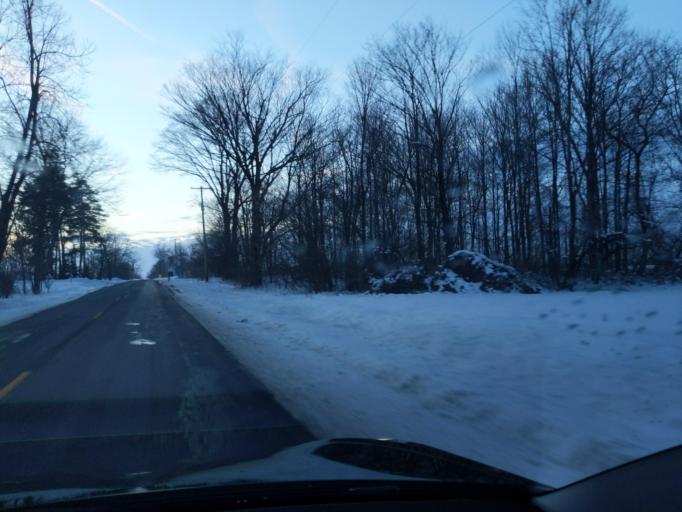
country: US
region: Michigan
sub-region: Ingham County
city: Mason
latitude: 42.5820
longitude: -84.3785
